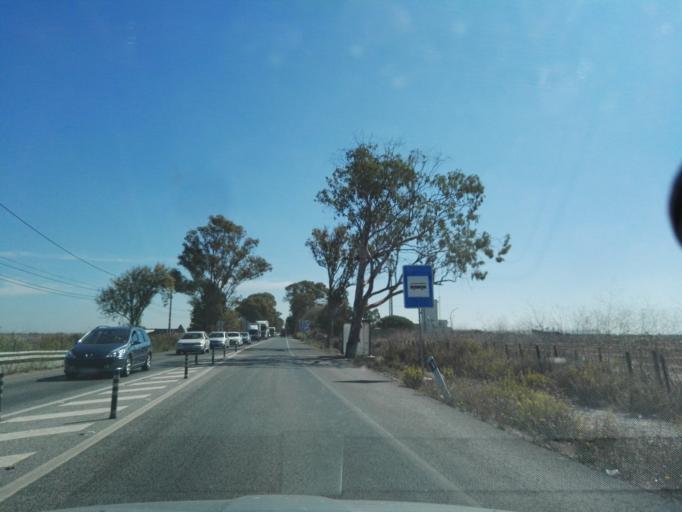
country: PT
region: Lisbon
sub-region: Vila Franca de Xira
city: Vila Franca de Xira
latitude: 38.9419
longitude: -8.9446
